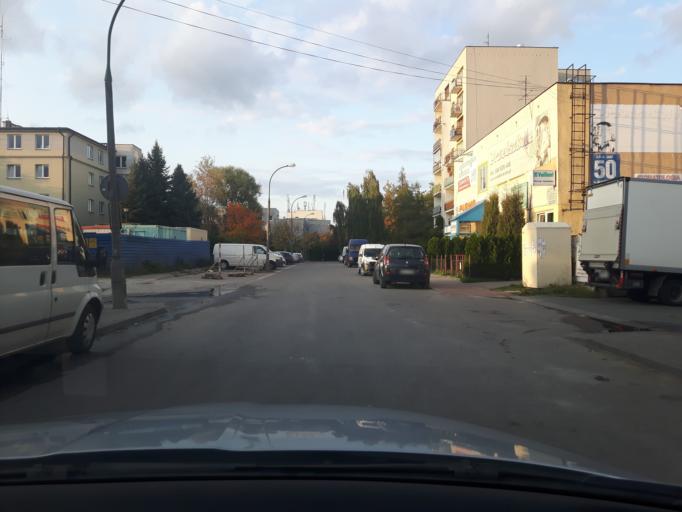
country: PL
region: Masovian Voivodeship
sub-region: Warszawa
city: Ursynow
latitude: 52.1534
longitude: 21.0199
